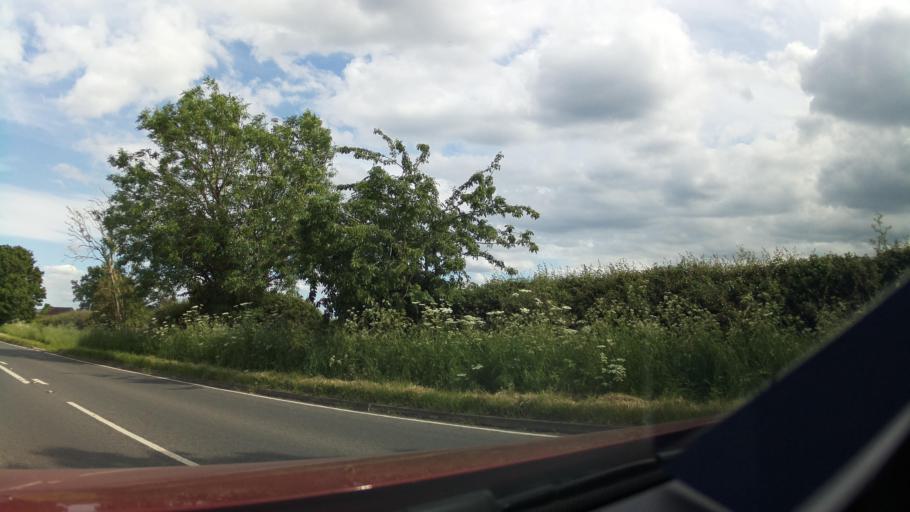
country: GB
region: England
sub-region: Worcestershire
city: Pershore
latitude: 52.0982
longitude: -2.0145
